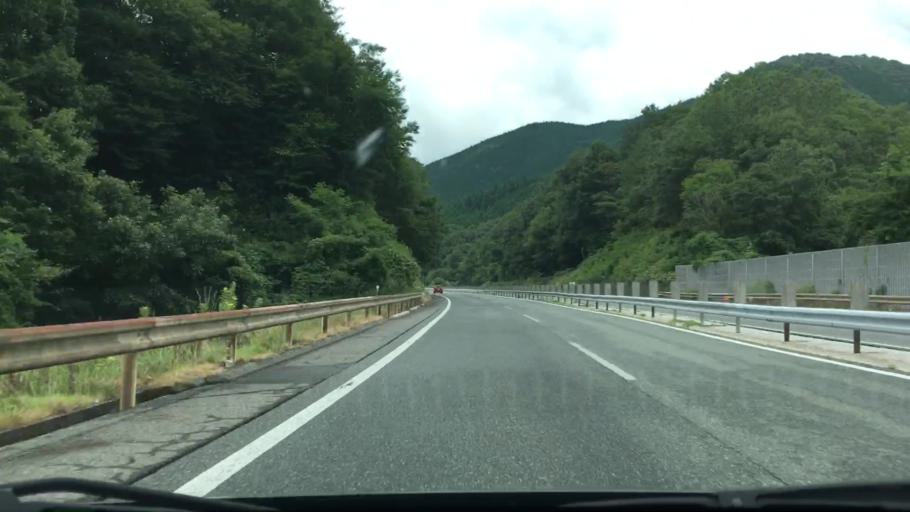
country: JP
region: Okayama
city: Niimi
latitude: 34.9605
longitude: 133.3317
